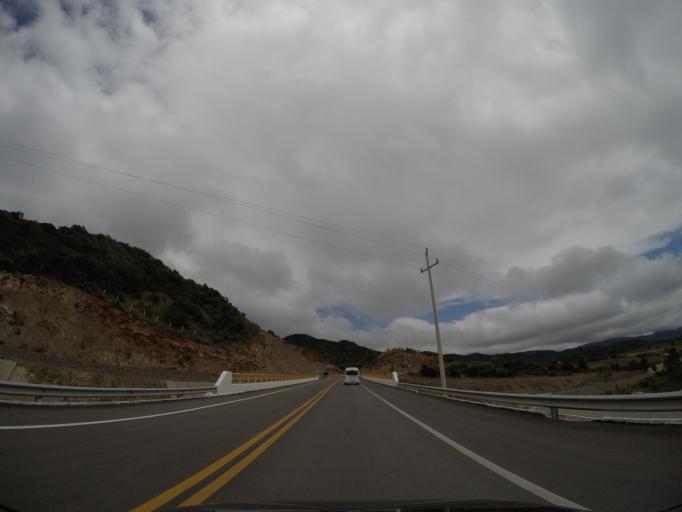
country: MX
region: Oaxaca
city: San Lorenzo Albarradas
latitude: 16.9236
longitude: -96.2558
